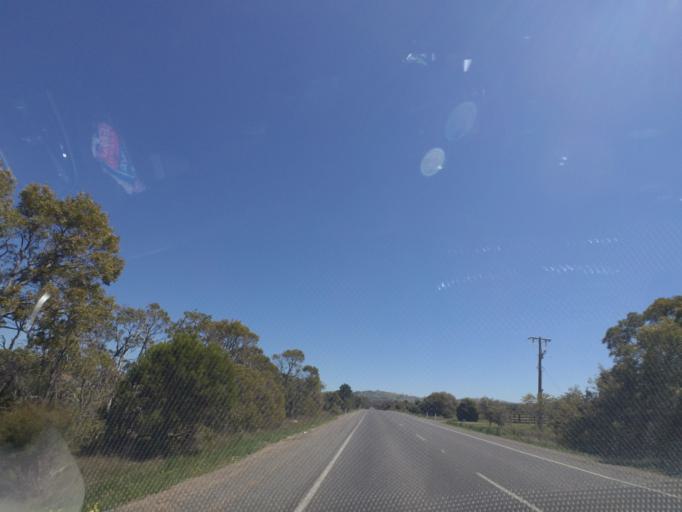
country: AU
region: Victoria
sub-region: Hume
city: Sunbury
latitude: -37.3069
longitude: 144.8387
